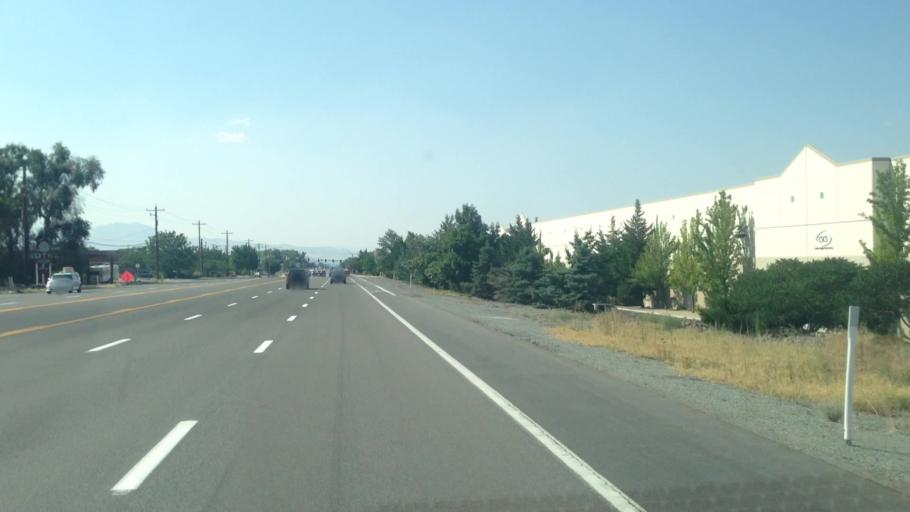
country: US
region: Nevada
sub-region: Washoe County
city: Sparks
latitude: 39.4157
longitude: -119.7543
